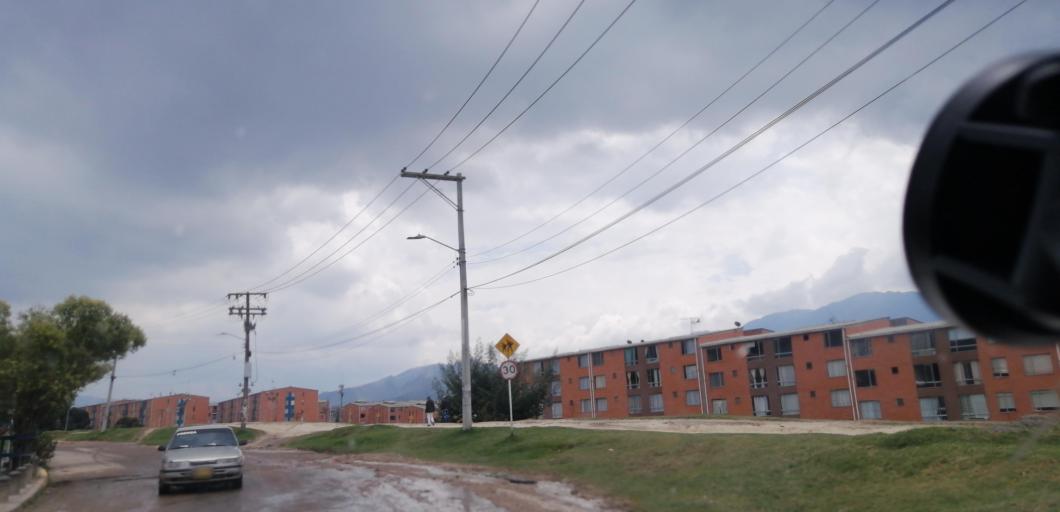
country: CO
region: Bogota D.C.
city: Bogota
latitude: 4.5312
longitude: -74.1151
